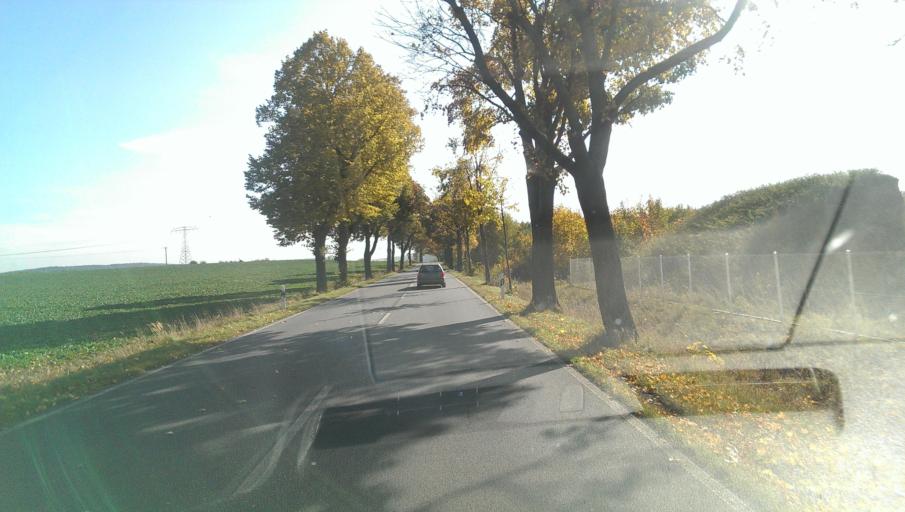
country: DE
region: Saxony
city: Dohma
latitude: 50.9211
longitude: 13.9382
